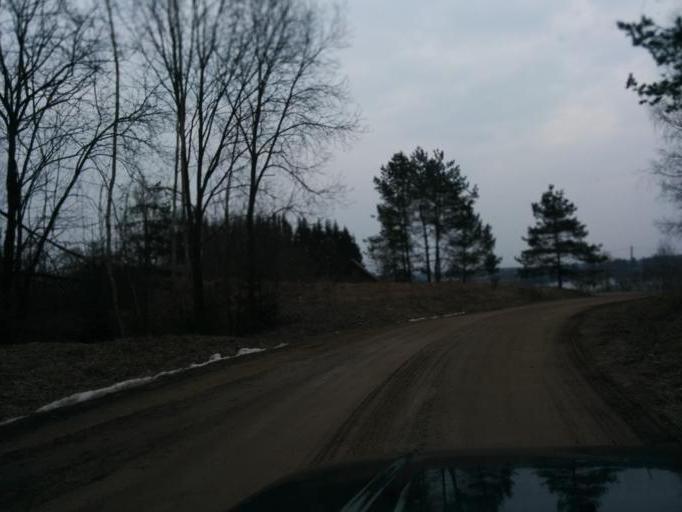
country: LV
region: Ogre
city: Ogre
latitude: 56.7844
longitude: 24.6105
